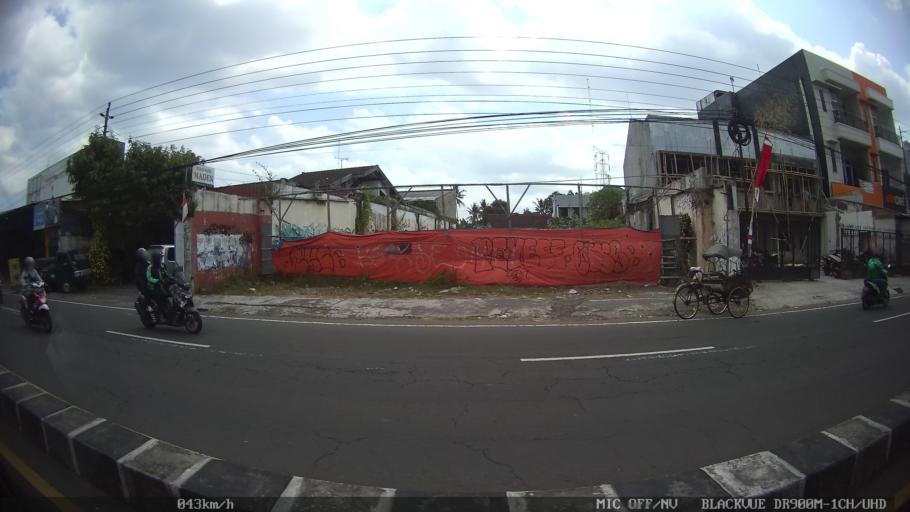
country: ID
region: Daerah Istimewa Yogyakarta
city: Melati
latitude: -7.7562
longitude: 110.3621
